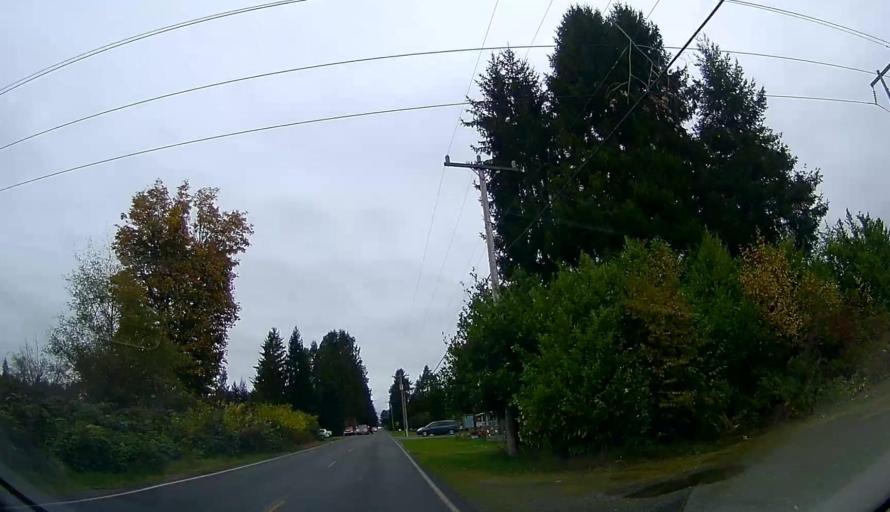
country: US
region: Washington
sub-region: Skagit County
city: Sedro-Woolley
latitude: 48.5032
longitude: -122.2054
